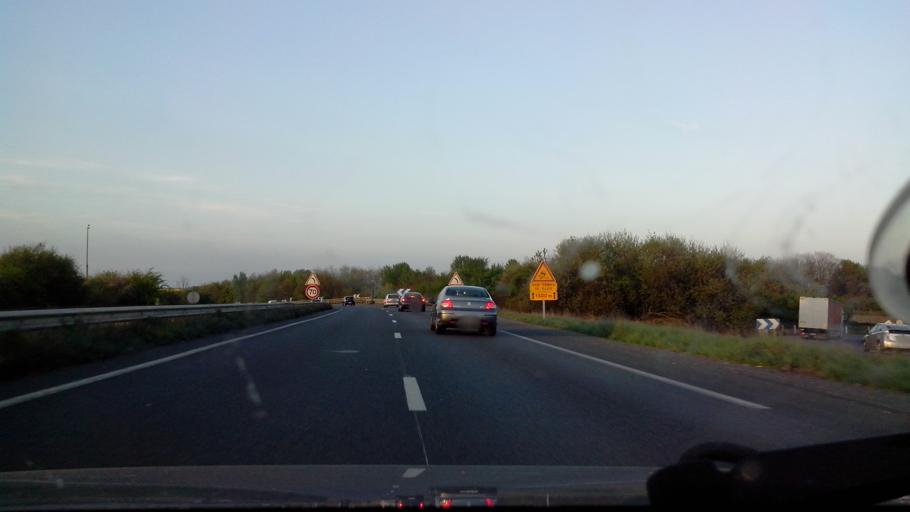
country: FR
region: Ile-de-France
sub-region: Departement de Seine-et-Marne
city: Moissy-Cramayel
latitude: 48.6530
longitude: 2.6143
